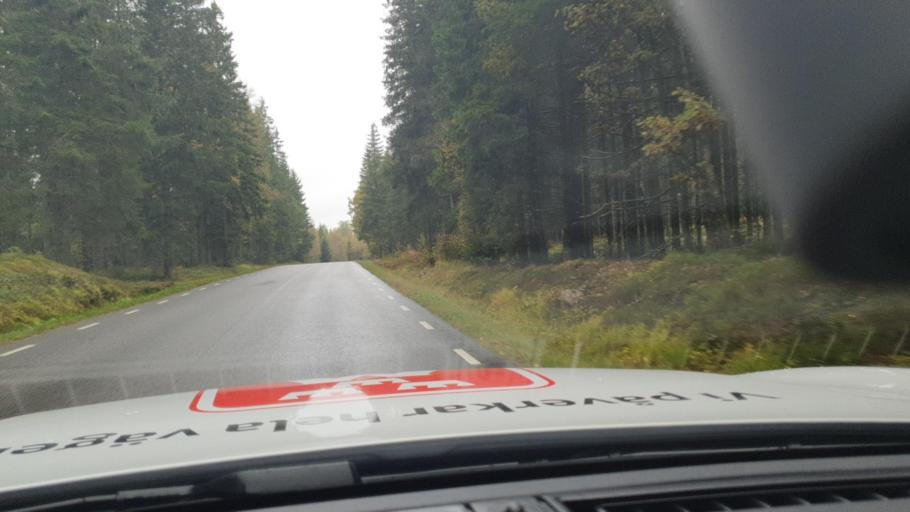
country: SE
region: Vaestra Goetaland
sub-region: Svenljunga Kommun
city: Svenljunga
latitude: 57.2503
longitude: 12.9387
